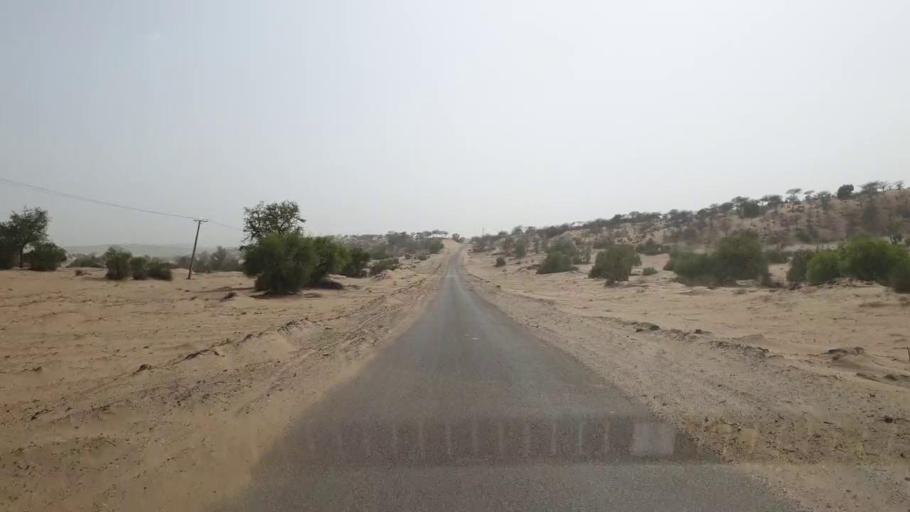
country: PK
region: Sindh
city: Mithi
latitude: 24.6197
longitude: 69.8935
